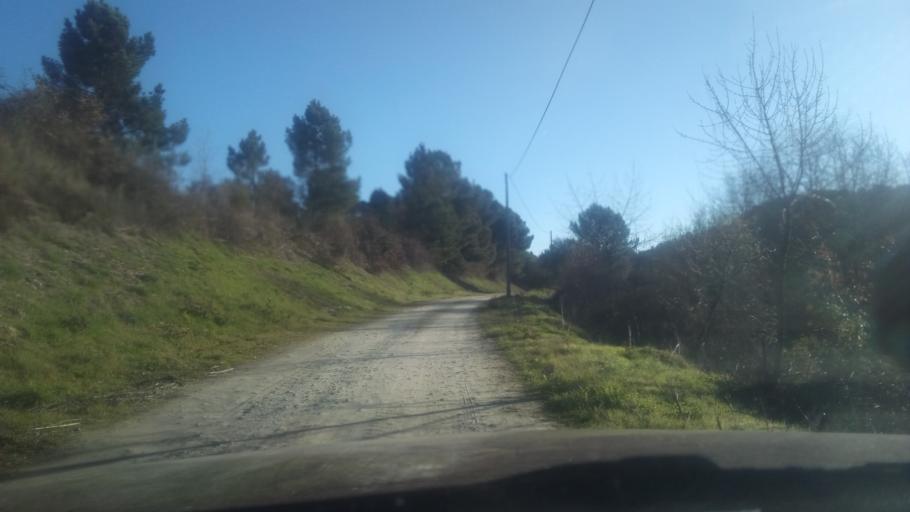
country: PT
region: Guarda
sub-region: Fornos de Algodres
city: Fornos de Algodres
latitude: 40.6118
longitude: -7.5235
